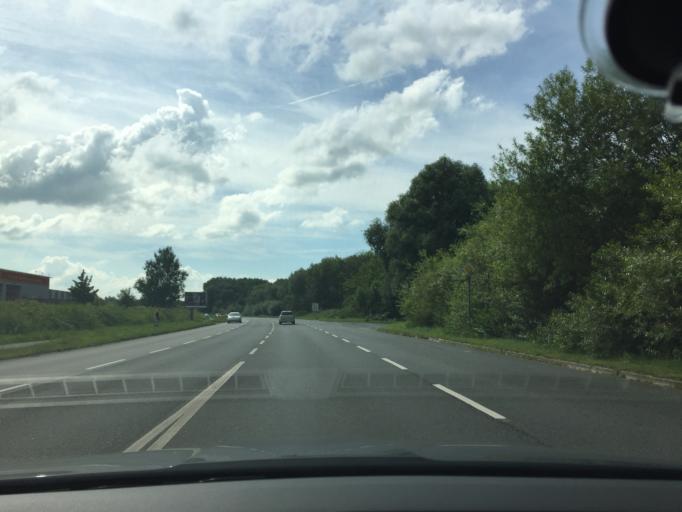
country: DE
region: Lower Saxony
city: Wilhelmshaven
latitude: 53.5237
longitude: 8.0856
